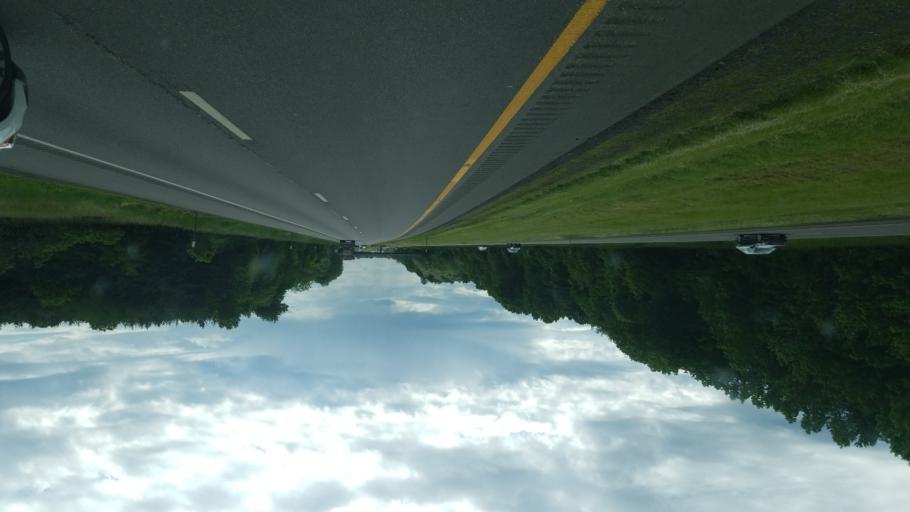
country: US
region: New York
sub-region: Ontario County
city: Geneva
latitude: 42.9597
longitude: -76.9431
